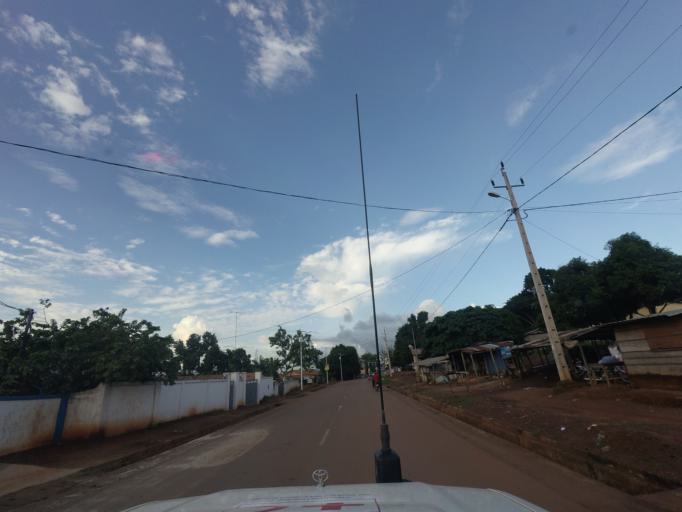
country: GN
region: Nzerekore
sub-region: Nzerekore Prefecture
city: Nzerekore
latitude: 7.7387
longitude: -8.8203
